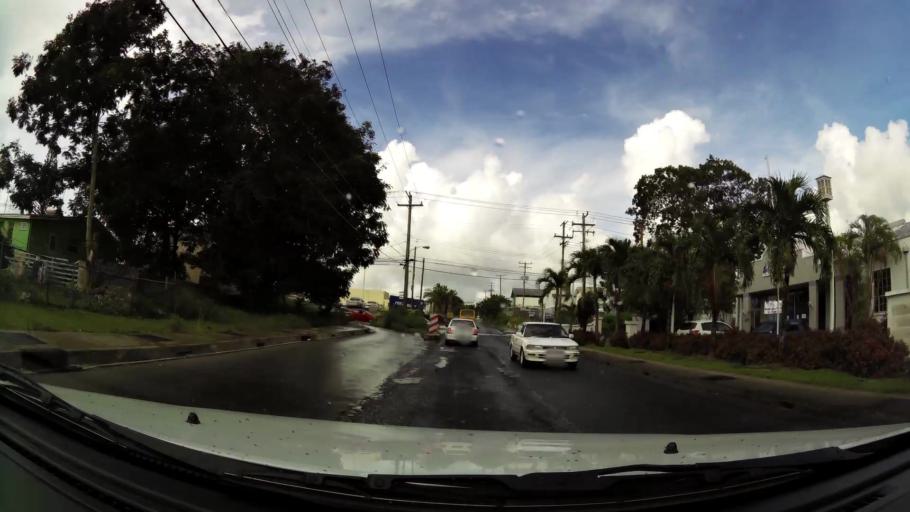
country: BB
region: Saint Michael
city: Bridgetown
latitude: 13.1386
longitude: -59.6067
